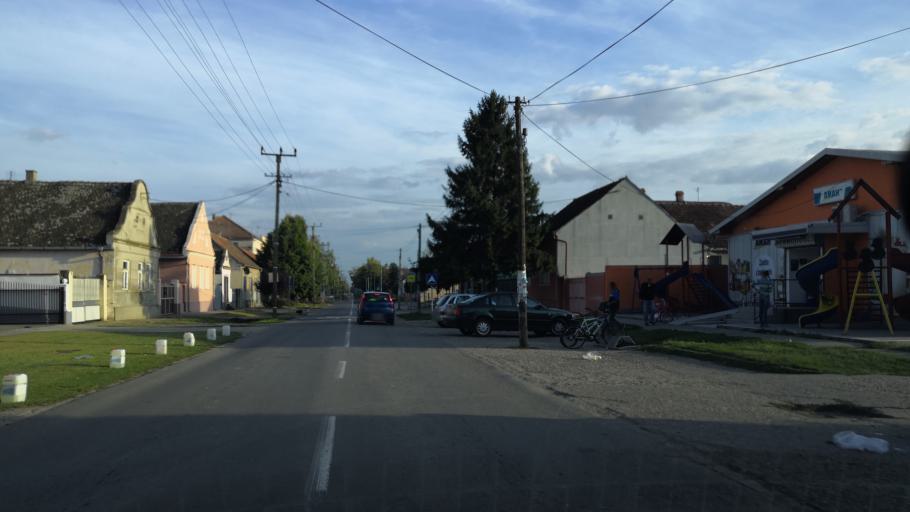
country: RS
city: Novi Karlovci
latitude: 45.0797
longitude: 20.1781
